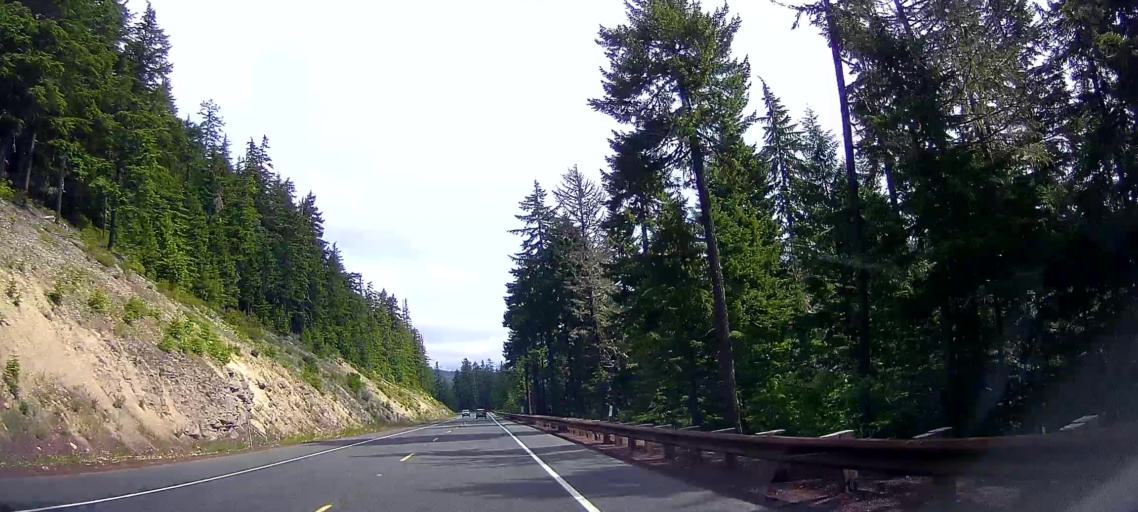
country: US
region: Oregon
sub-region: Clackamas County
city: Mount Hood Village
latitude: 45.2146
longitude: -121.6982
